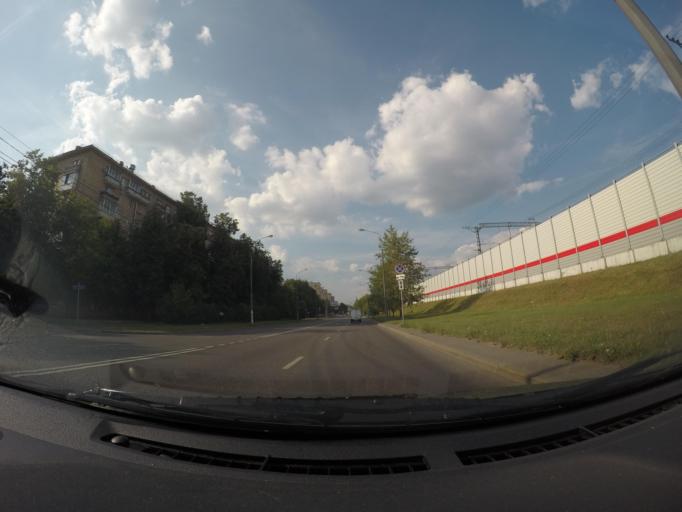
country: RU
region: Moskovskaya
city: Bogorodskoye
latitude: 55.7789
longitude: 37.7433
